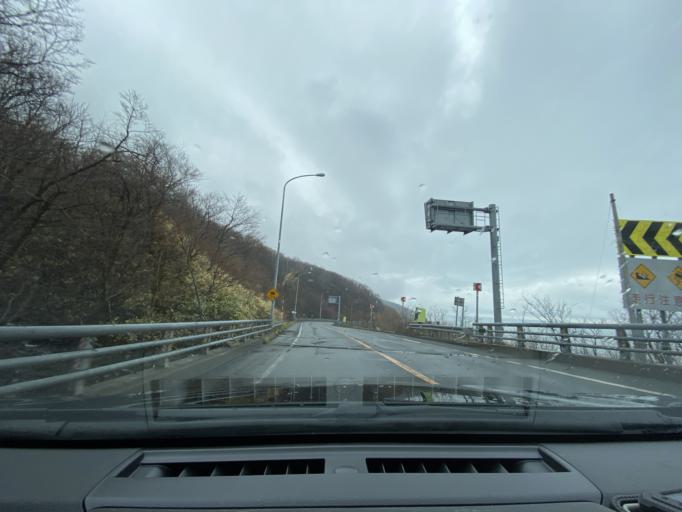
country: JP
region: Hokkaido
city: Rumoi
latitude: 43.8179
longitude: 141.4233
